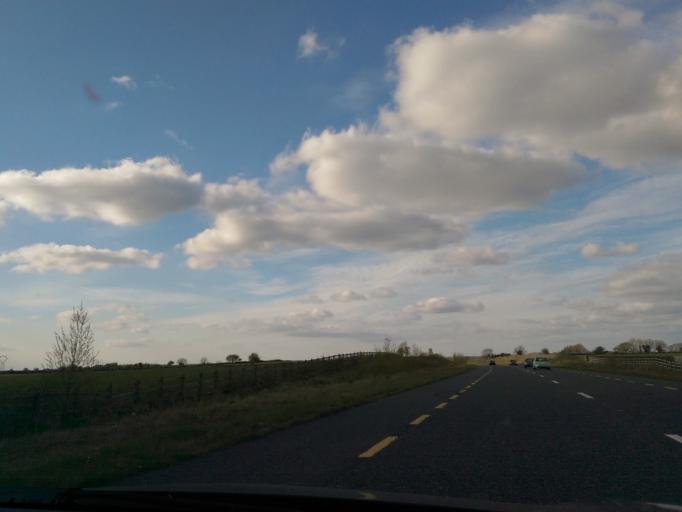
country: IE
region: Connaught
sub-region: County Galway
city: Loughrea
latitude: 53.2447
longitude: -8.5938
